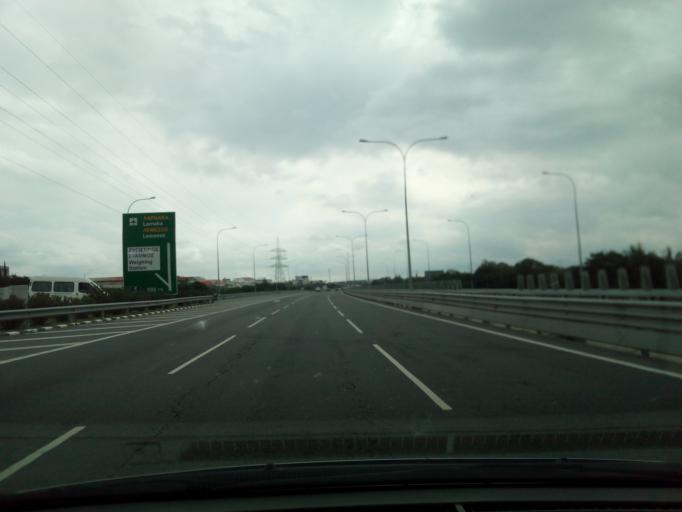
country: CY
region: Lefkosia
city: Geri
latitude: 35.0818
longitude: 33.3770
